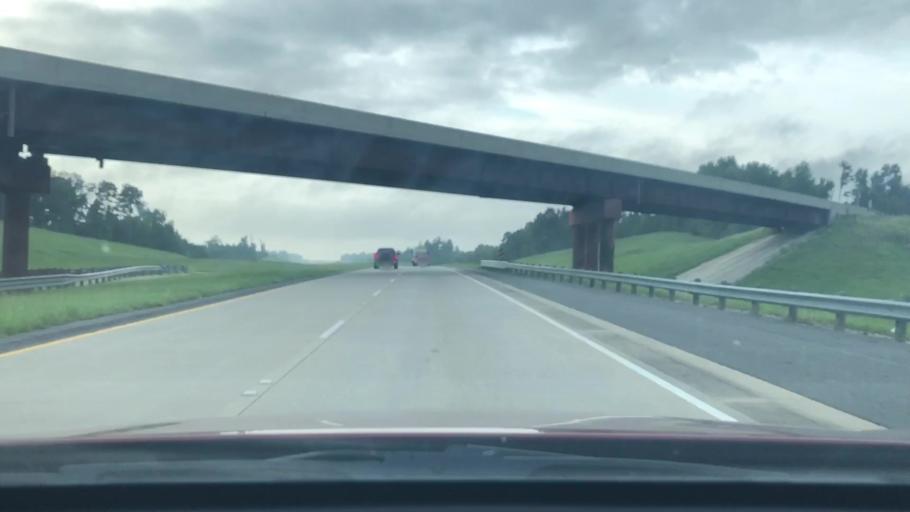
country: US
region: Louisiana
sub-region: Caddo Parish
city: Vivian
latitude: 32.9785
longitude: -93.9101
